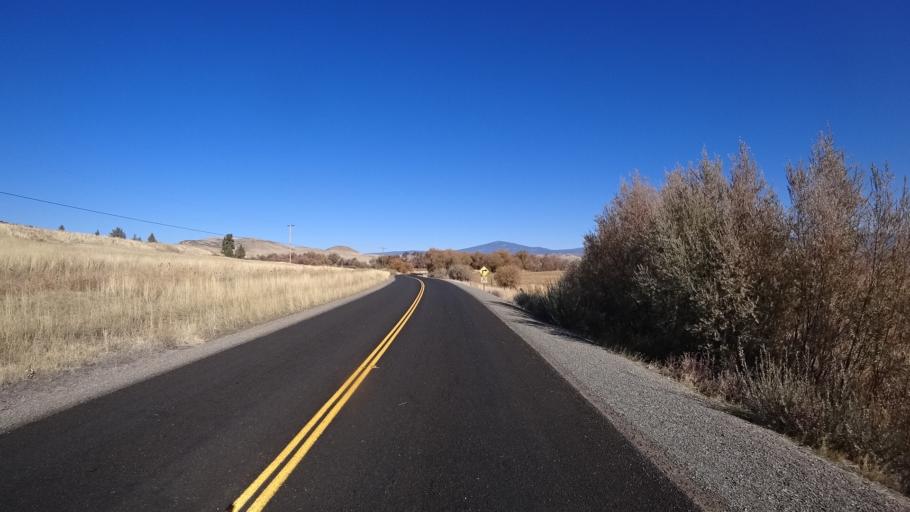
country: US
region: California
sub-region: Siskiyou County
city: Montague
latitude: 41.7248
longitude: -122.4329
